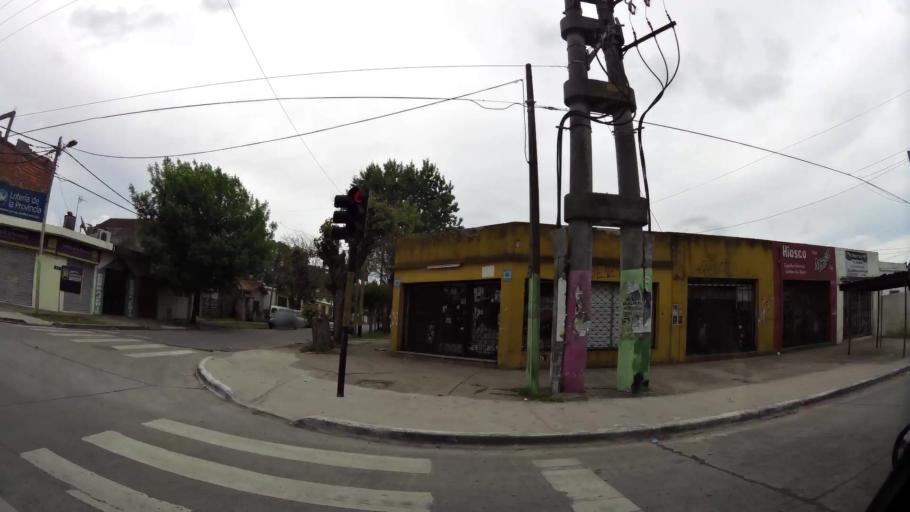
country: AR
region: Buenos Aires
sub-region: Partido de Quilmes
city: Quilmes
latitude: -34.7591
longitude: -58.2717
